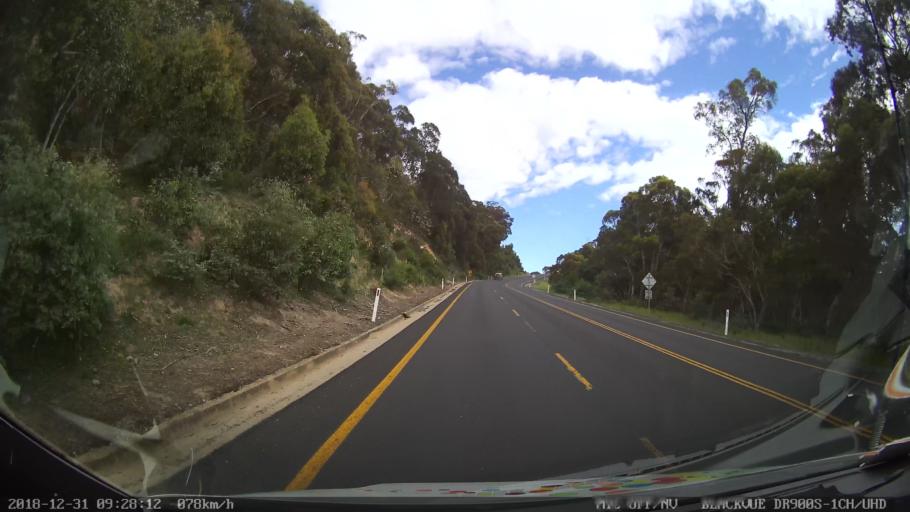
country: AU
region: New South Wales
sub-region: Snowy River
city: Jindabyne
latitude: -36.4581
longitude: 148.4757
